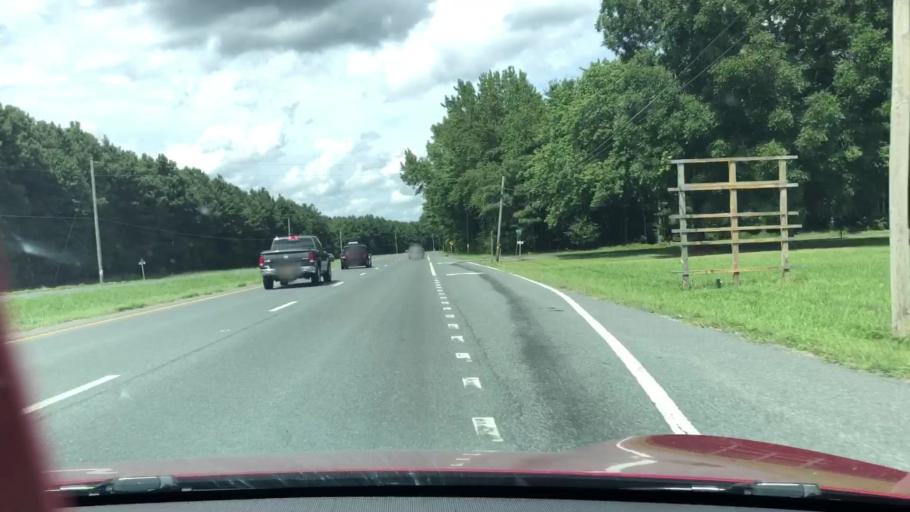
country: US
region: Virginia
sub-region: Accomack County
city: Wattsville
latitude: 37.8749
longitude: -75.5584
